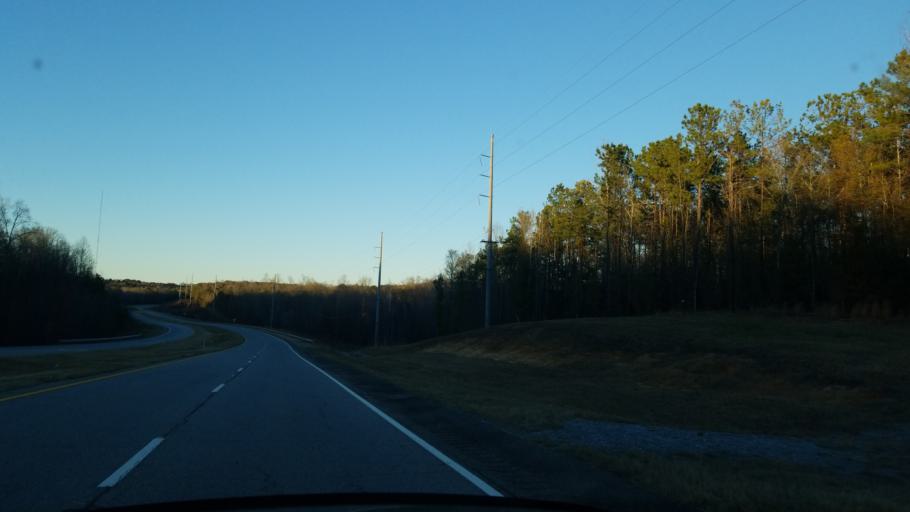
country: US
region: Georgia
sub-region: Chattahoochee County
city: Cusseta
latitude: 32.2890
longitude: -84.7780
